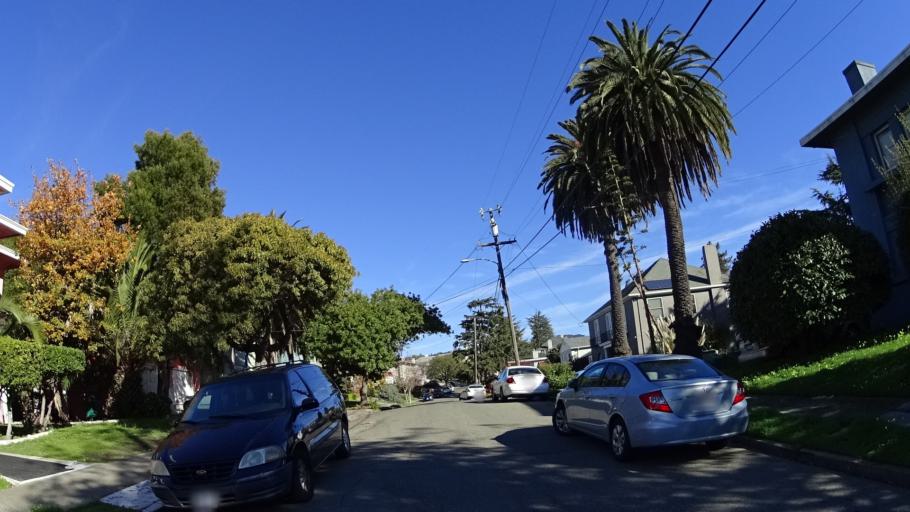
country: US
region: California
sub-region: Alameda County
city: Piedmont
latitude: 37.8129
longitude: -122.2354
